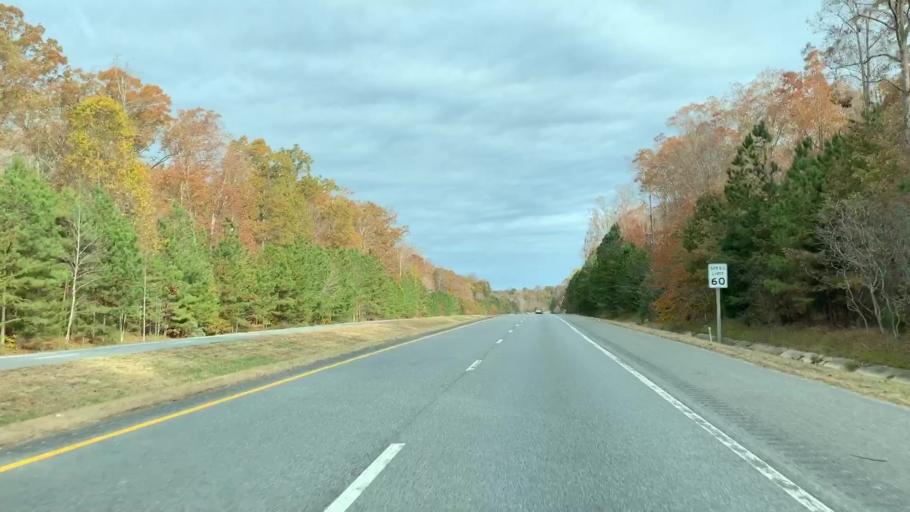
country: US
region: Virginia
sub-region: James City County
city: Williamsburg
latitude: 37.2832
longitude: -76.7533
